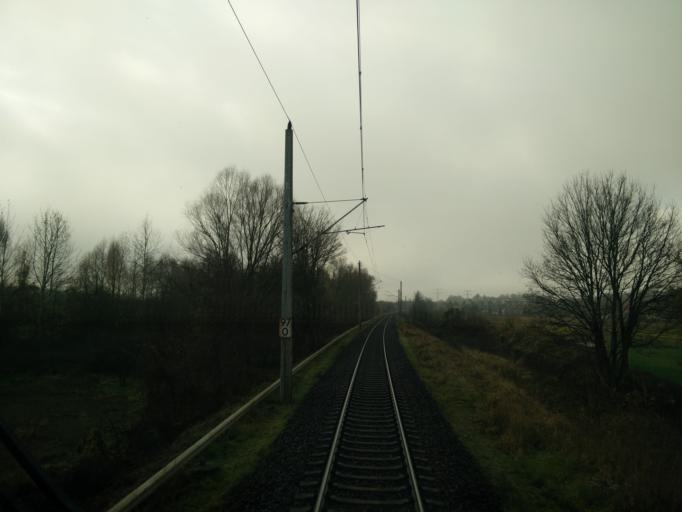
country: DE
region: Mecklenburg-Vorpommern
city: Wismar
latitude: 53.8856
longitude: 11.4758
